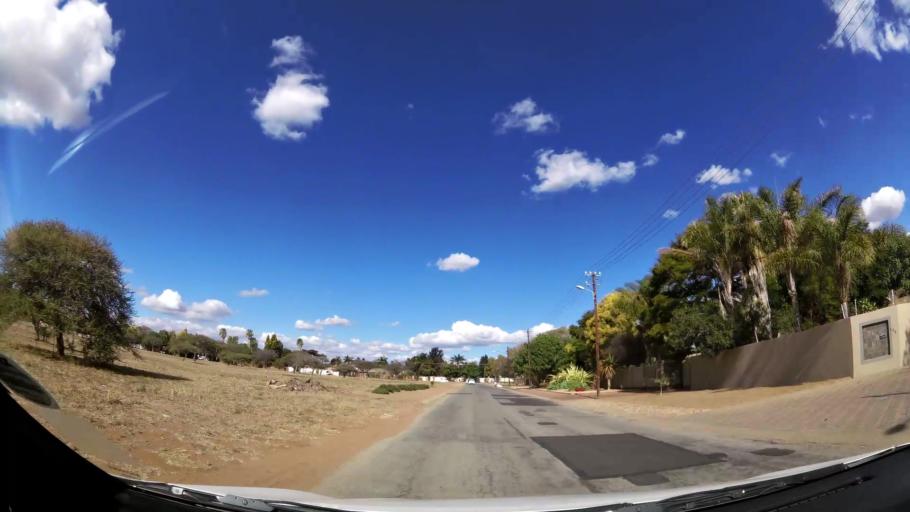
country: ZA
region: Limpopo
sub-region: Capricorn District Municipality
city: Polokwane
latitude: -23.8860
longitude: 29.4639
